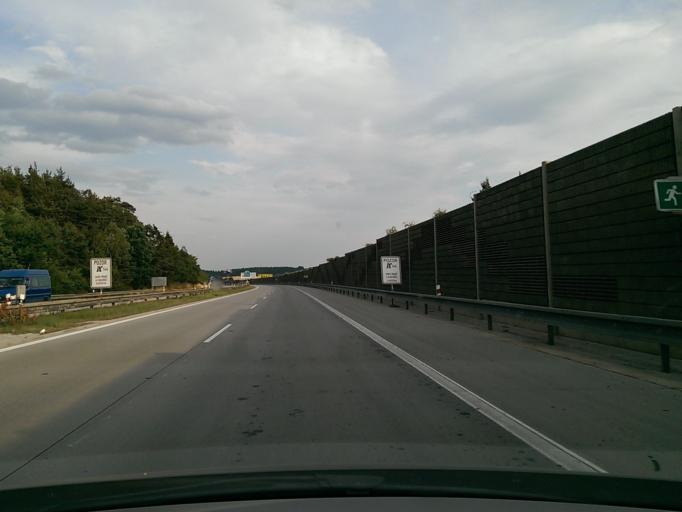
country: CZ
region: Vysocina
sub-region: Okres Zd'ar nad Sazavou
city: Velke Mezirici
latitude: 49.3507
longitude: 16.0357
